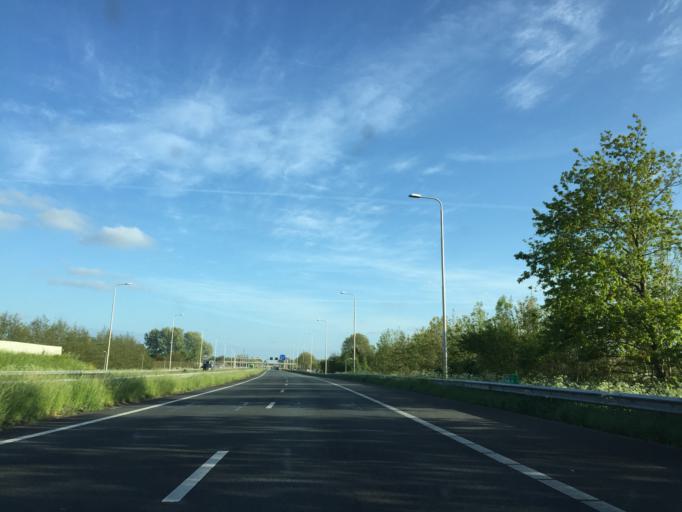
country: NL
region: North Holland
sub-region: Gemeente Hoorn
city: Hoorn
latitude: 52.6757
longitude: 5.0307
